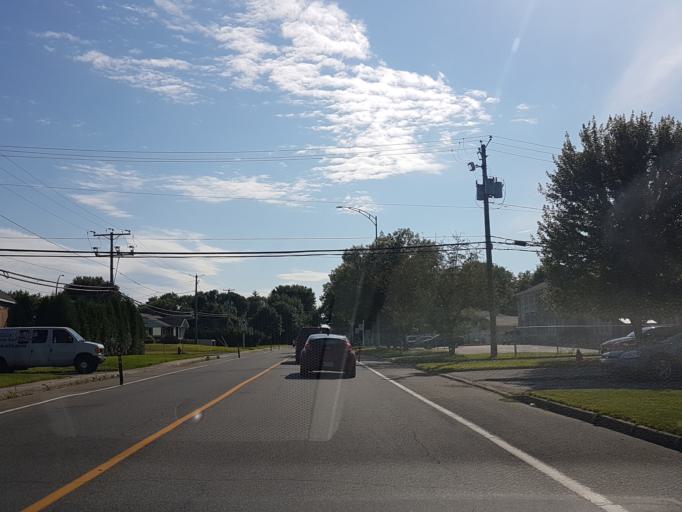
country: CA
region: Quebec
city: Sainte-Catherine
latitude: 46.3088
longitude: -72.5838
